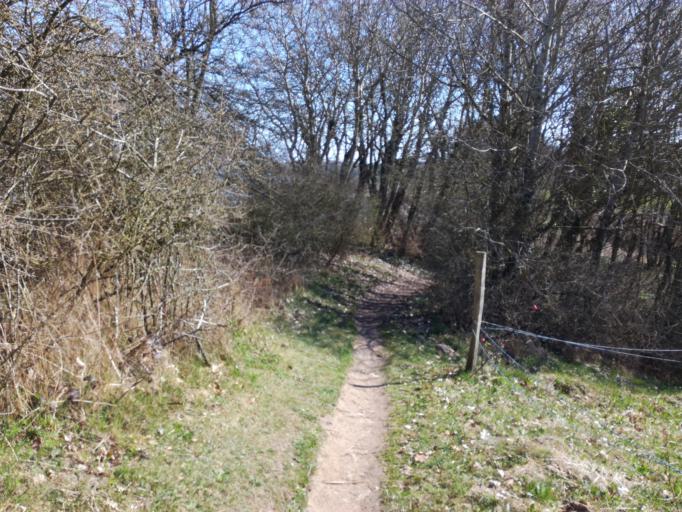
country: DK
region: South Denmark
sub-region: Fredericia Kommune
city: Fredericia
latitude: 55.6246
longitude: 9.8440
